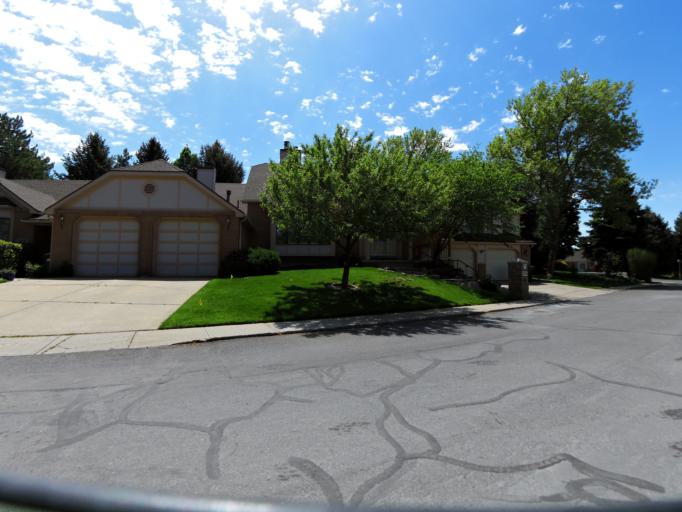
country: US
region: Utah
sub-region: Weber County
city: Uintah
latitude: 41.1763
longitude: -111.9344
